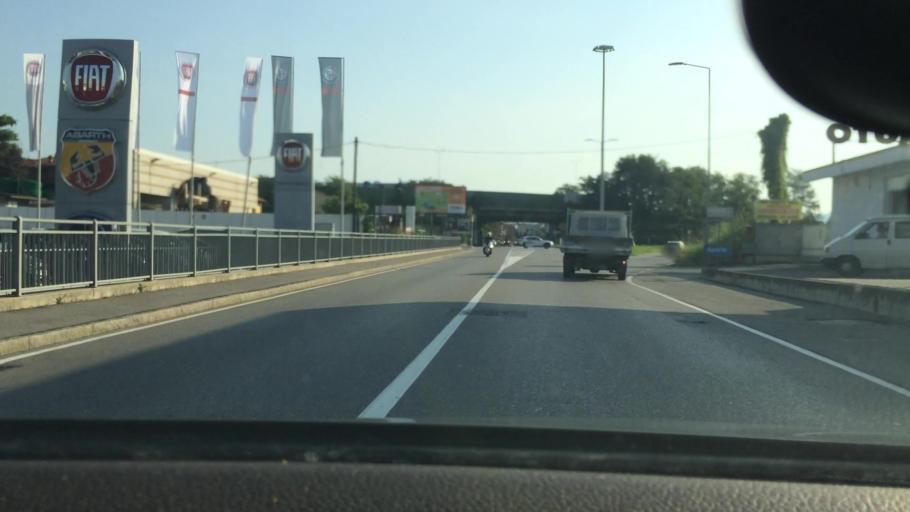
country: IT
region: Lombardy
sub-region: Provincia di Bergamo
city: Lallio
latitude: 45.6743
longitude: 9.6443
